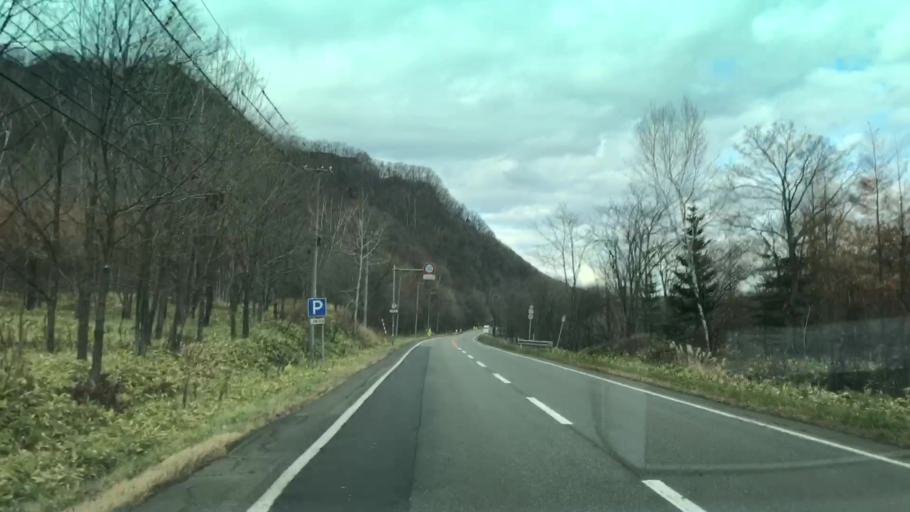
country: JP
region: Hokkaido
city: Shizunai-furukawacho
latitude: 42.8347
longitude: 142.4157
